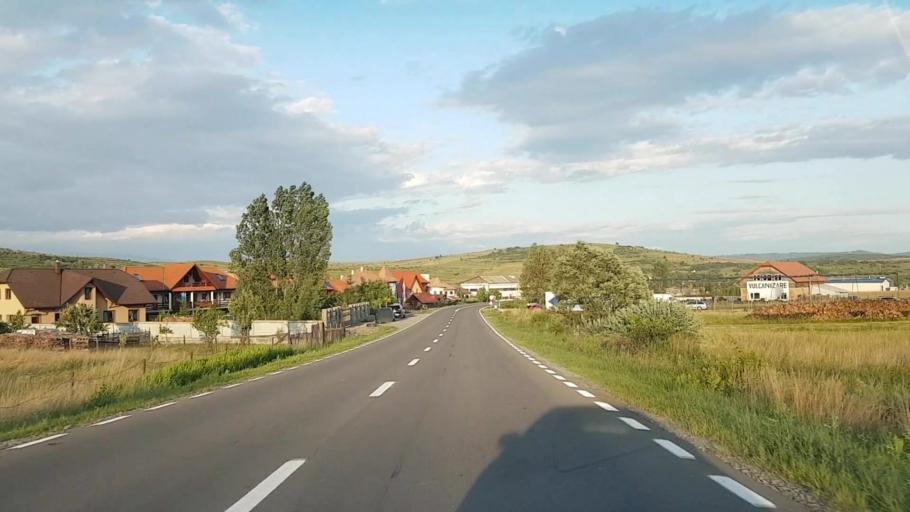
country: RO
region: Harghita
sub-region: Comuna Lupeni
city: Lupeni
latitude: 46.3706
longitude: 25.2269
